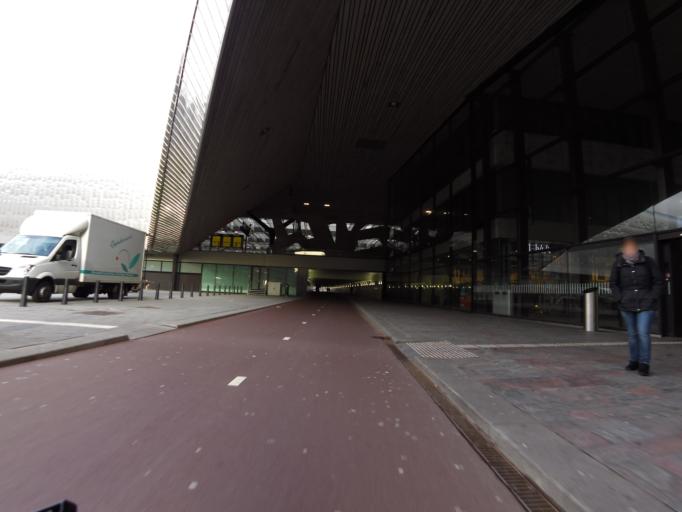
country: NL
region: South Holland
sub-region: Gemeente Rotterdam
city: Rotterdam
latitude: 51.9241
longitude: 4.4691
